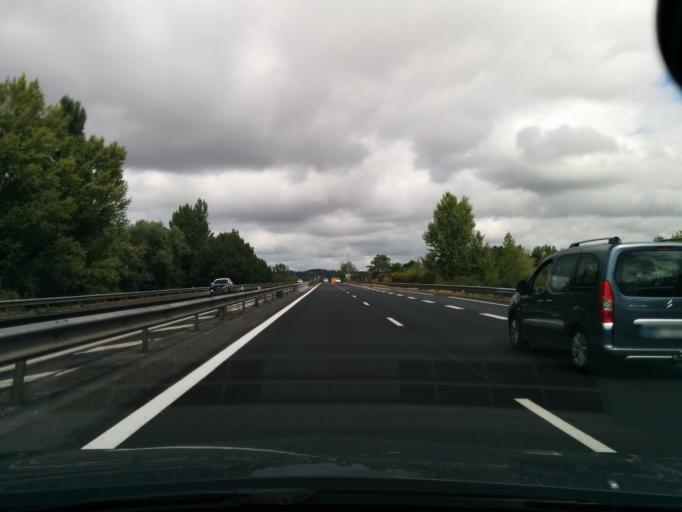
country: FR
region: Limousin
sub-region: Departement de la Correze
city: Saint-Pantaleon-de-Larche
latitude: 45.1517
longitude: 1.4841
